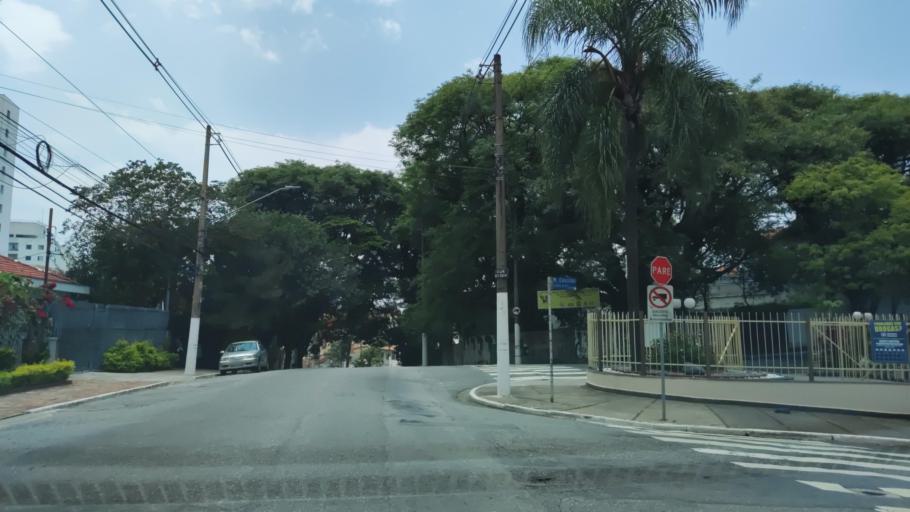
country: BR
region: Sao Paulo
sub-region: Sao Paulo
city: Sao Paulo
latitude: -23.5027
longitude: -46.6460
